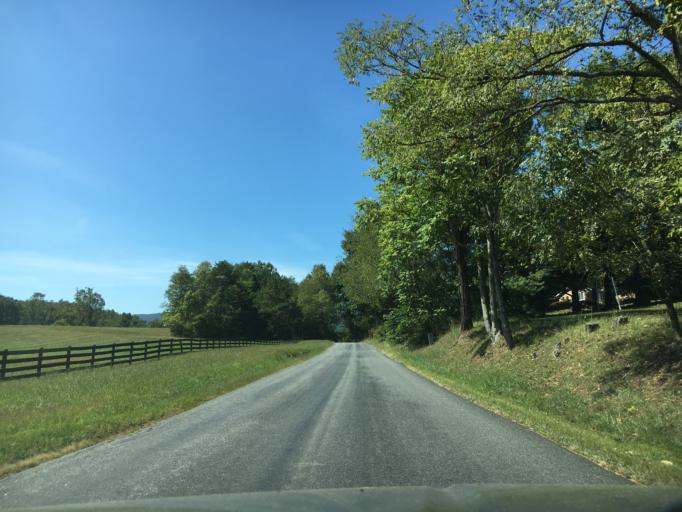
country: US
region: Virginia
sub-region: Albemarle County
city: Crozet
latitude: 38.0270
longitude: -78.7917
